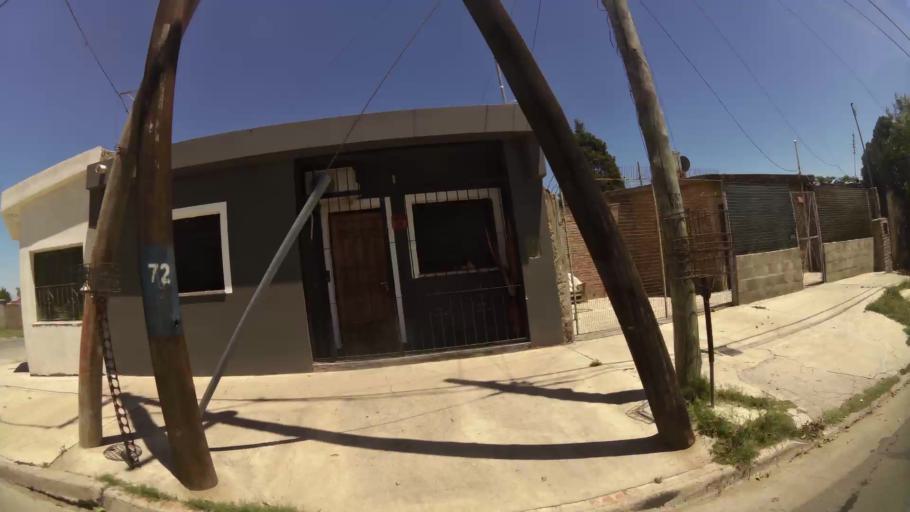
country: AR
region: Cordoba
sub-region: Departamento de Capital
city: Cordoba
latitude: -31.4213
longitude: -64.1193
